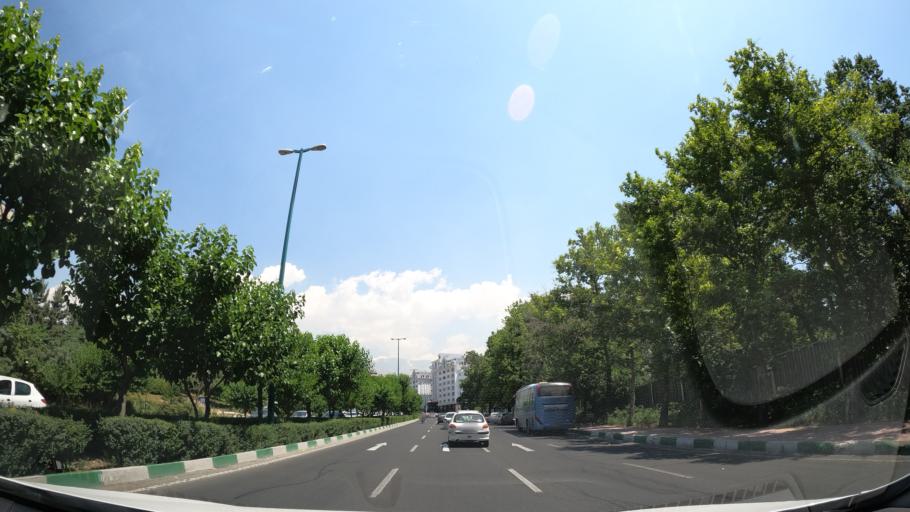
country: IR
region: Tehran
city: Tajrish
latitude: 35.7656
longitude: 51.3780
